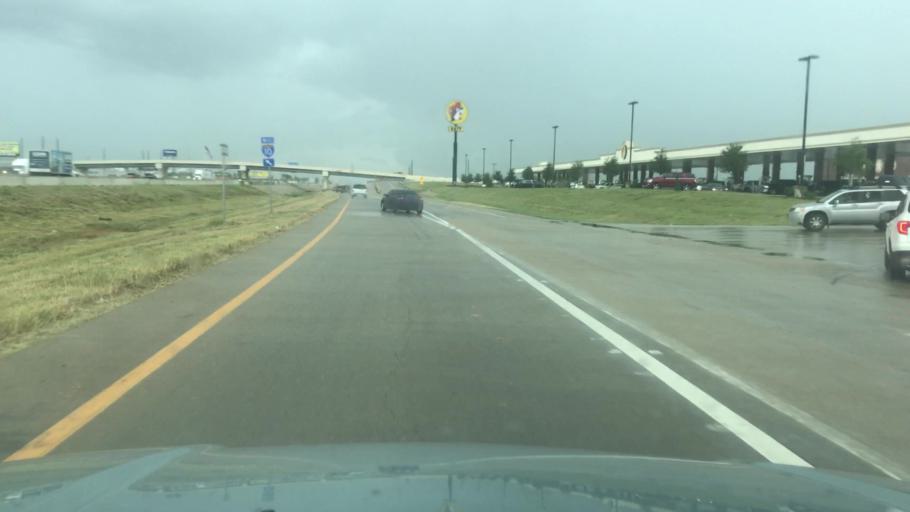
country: US
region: Texas
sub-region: Harris County
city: Katy
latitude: 29.7776
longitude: -95.8464
